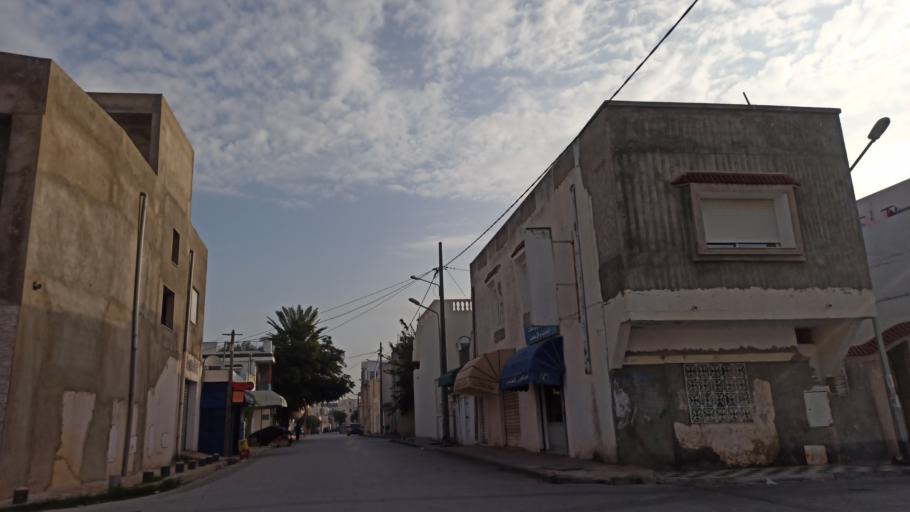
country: TN
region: Tunis
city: La Goulette
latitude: 36.8515
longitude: 10.2651
